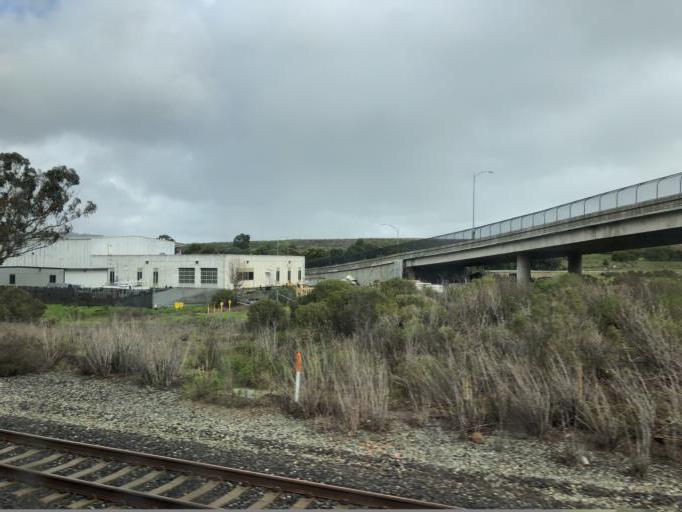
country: US
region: California
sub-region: San Mateo County
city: Brisbane
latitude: 37.6879
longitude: -122.3993
